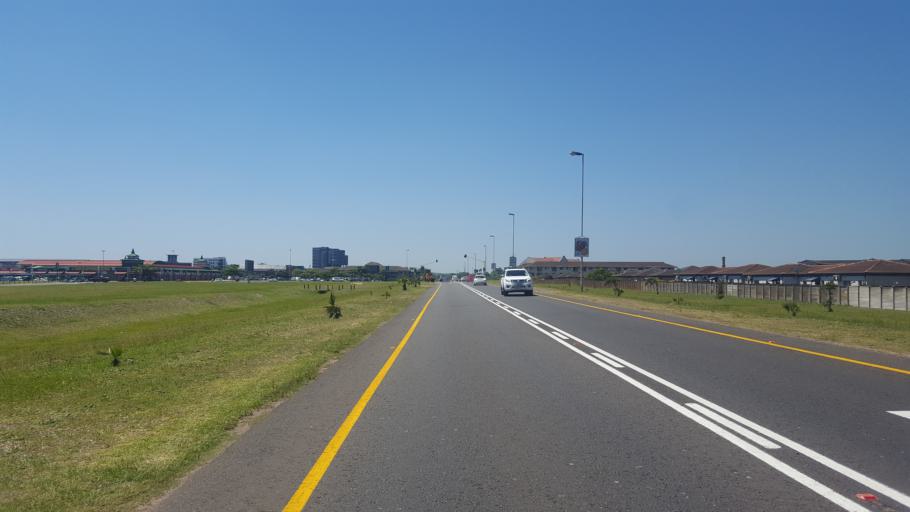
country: ZA
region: KwaZulu-Natal
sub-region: uThungulu District Municipality
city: Richards Bay
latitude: -28.7573
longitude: 32.0523
